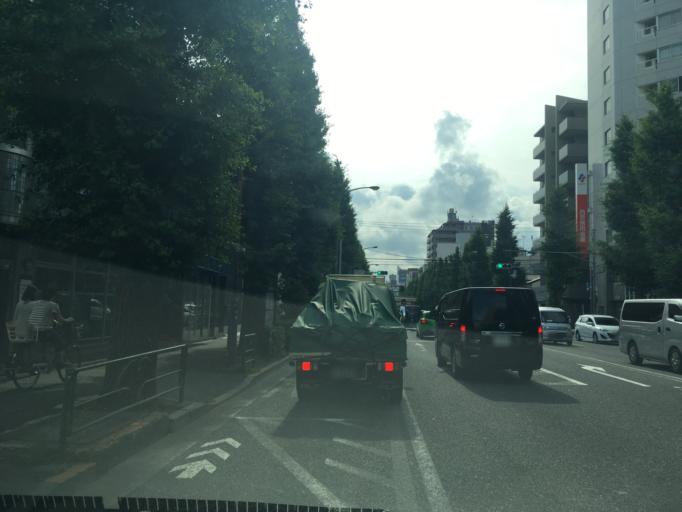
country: JP
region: Tokyo
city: Tokyo
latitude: 35.6978
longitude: 139.6432
